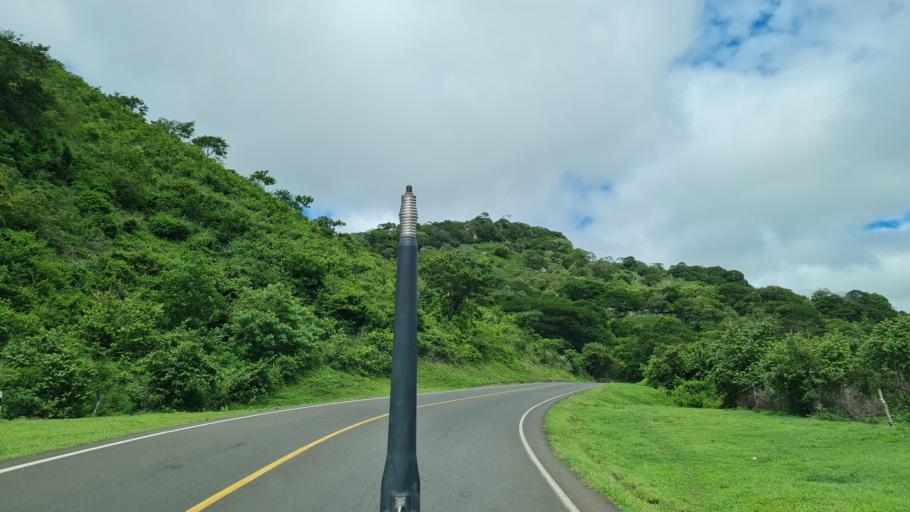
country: NI
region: Matagalpa
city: Terrabona
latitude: 12.5901
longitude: -85.9441
